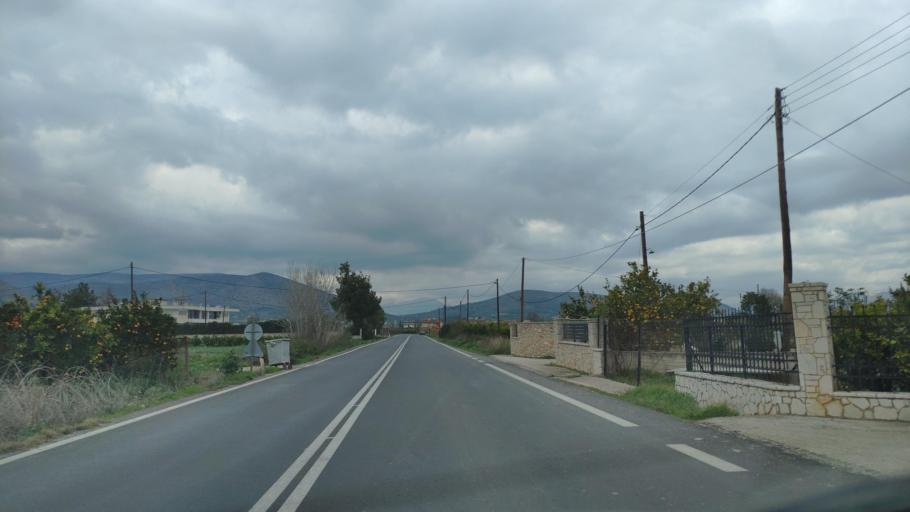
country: GR
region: Peloponnese
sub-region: Nomos Argolidos
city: Nea Kios
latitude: 37.5882
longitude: 22.7091
